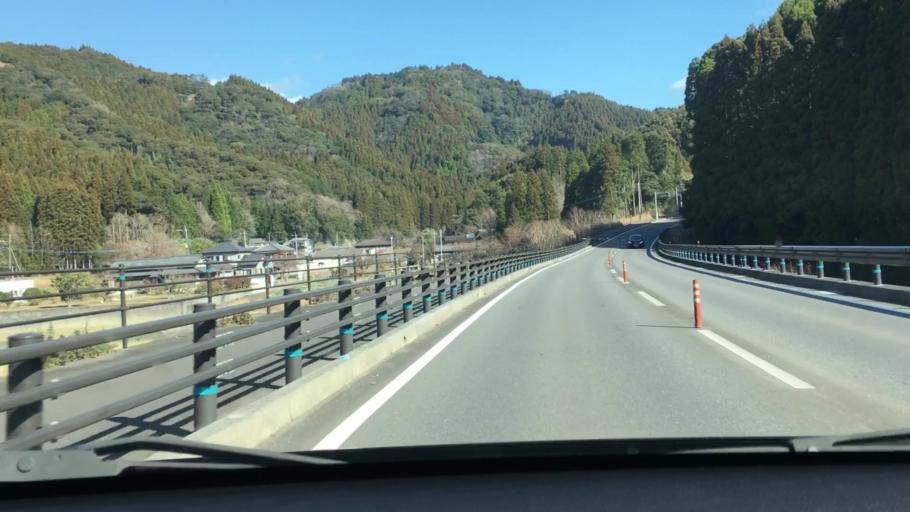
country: JP
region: Oita
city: Saiki
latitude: 32.9590
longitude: 131.8467
